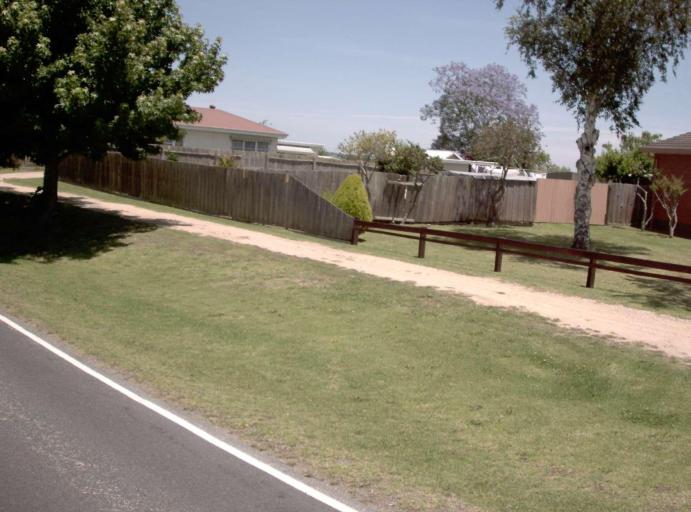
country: AU
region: Victoria
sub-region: East Gippsland
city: Lakes Entrance
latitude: -37.7055
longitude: 147.8339
